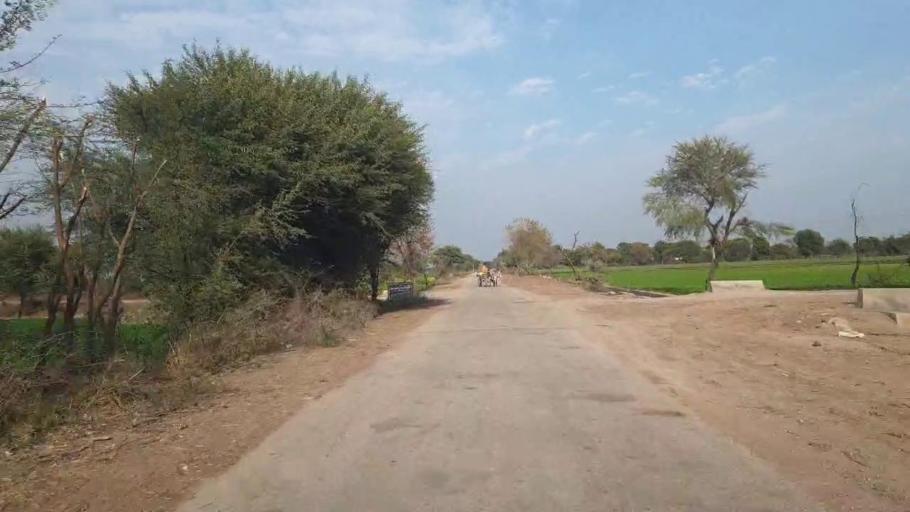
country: PK
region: Sindh
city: Shahdadpur
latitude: 26.0470
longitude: 68.5641
